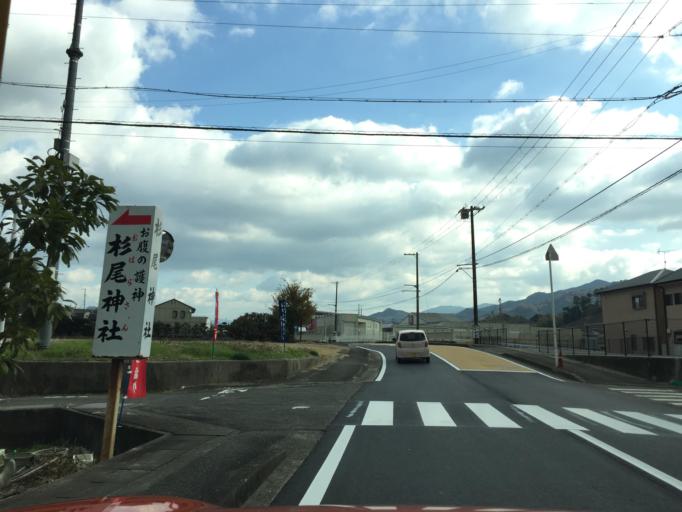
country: JP
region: Wakayama
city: Kainan
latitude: 34.1609
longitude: 135.2629
